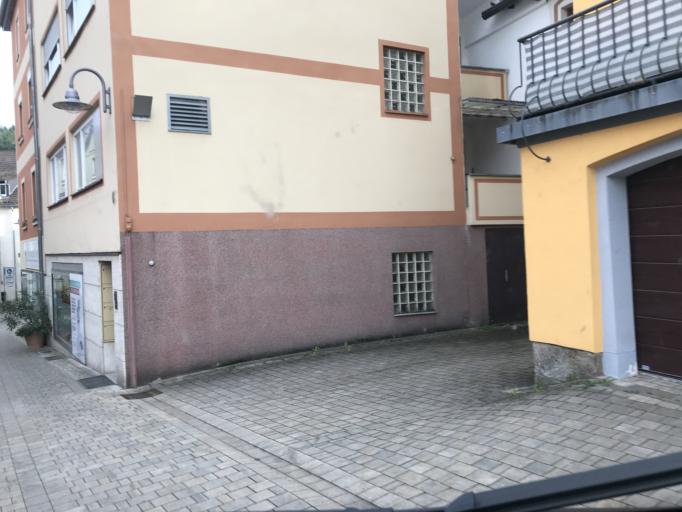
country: DE
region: Bavaria
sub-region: Regierungsbezirk Unterfranken
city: Bad Bruckenau
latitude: 50.3108
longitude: 9.7920
